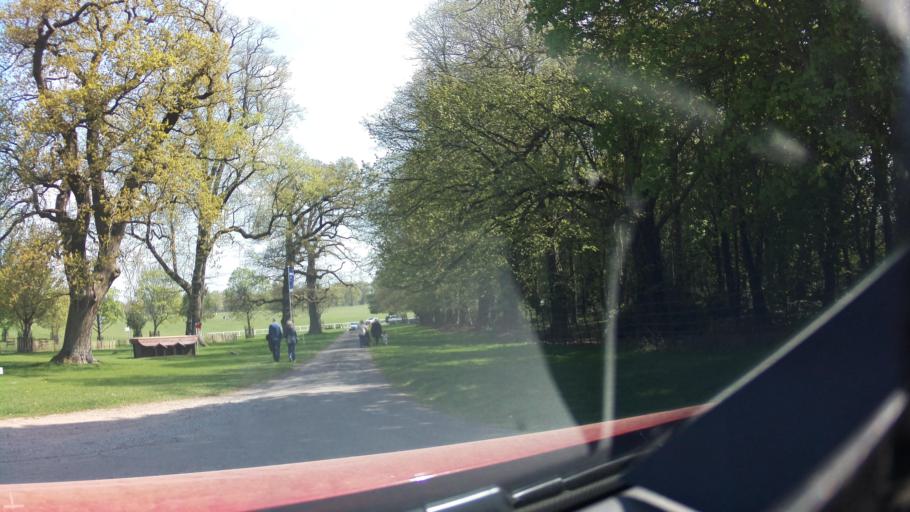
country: GB
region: England
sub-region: Wiltshire
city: Luckington
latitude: 51.5457
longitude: -2.2850
